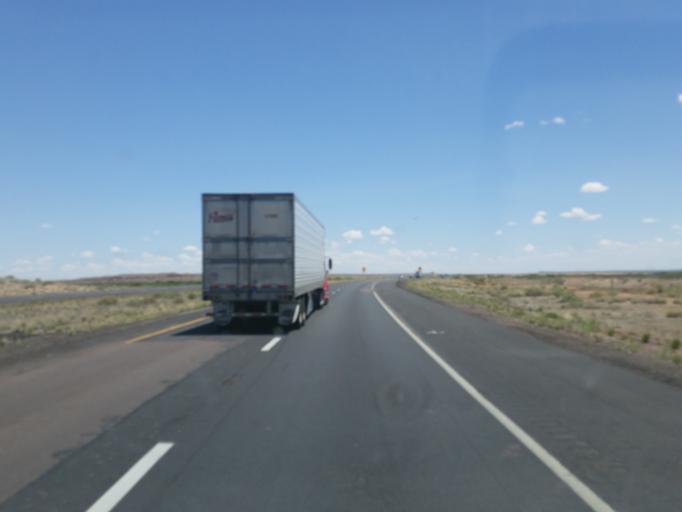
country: US
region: Arizona
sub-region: Navajo County
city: Winslow
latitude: 35.0063
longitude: -110.6180
